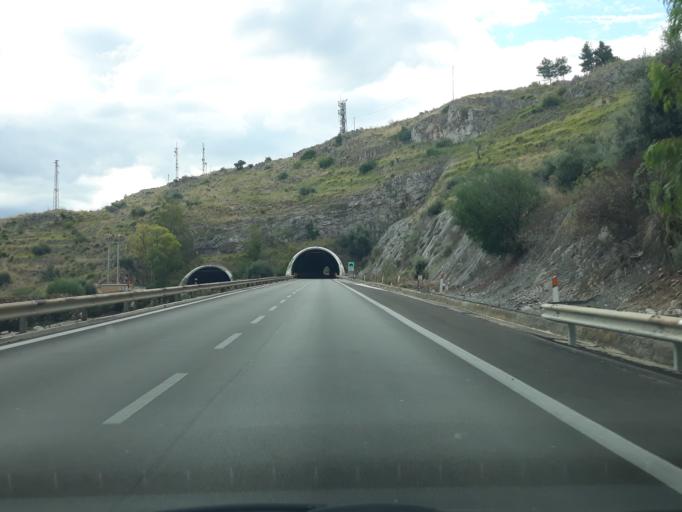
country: IT
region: Sicily
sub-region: Palermo
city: Trabia
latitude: 37.9951
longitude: 13.6487
